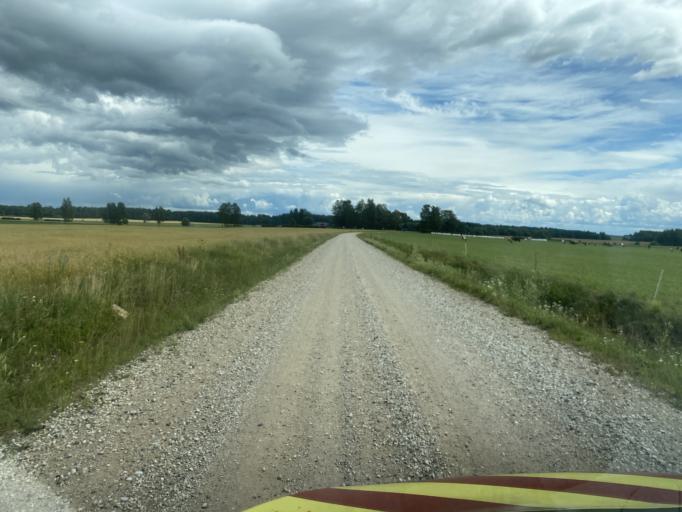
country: EE
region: Valgamaa
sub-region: Torva linn
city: Torva
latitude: 57.9536
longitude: 25.9627
